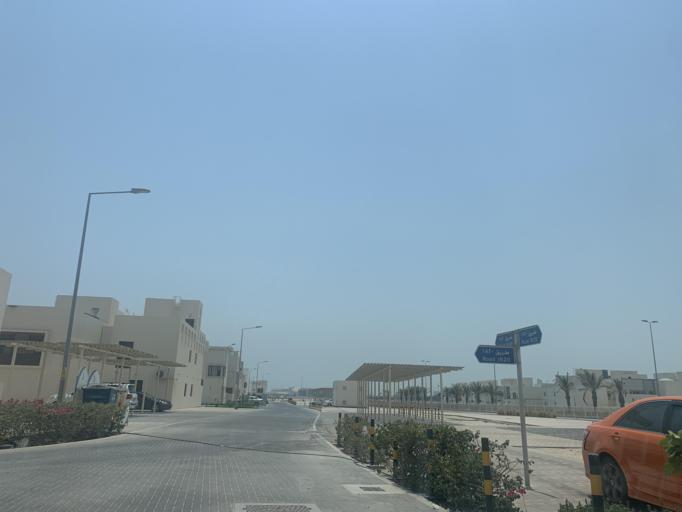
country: BH
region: Muharraq
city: Al Hadd
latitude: 26.2341
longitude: 50.6695
